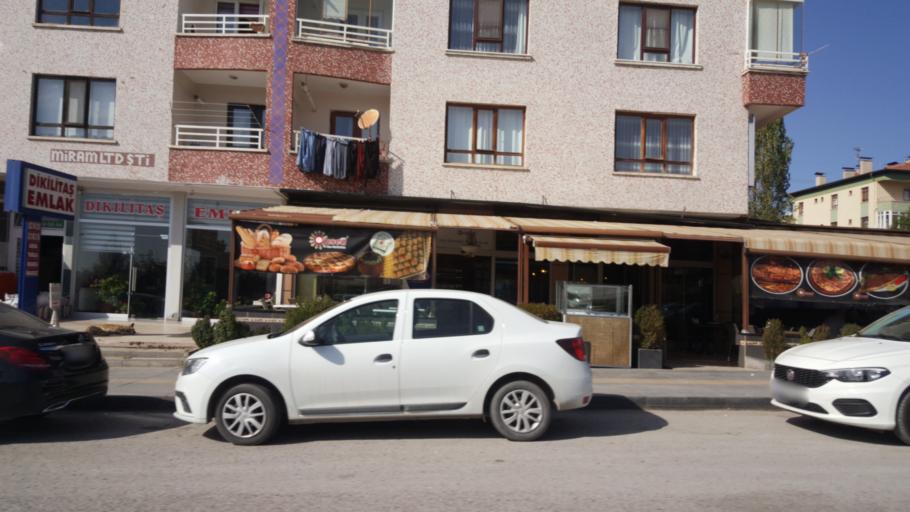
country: TR
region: Ankara
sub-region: Goelbasi
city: Golbasi
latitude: 39.8047
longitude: 32.8022
